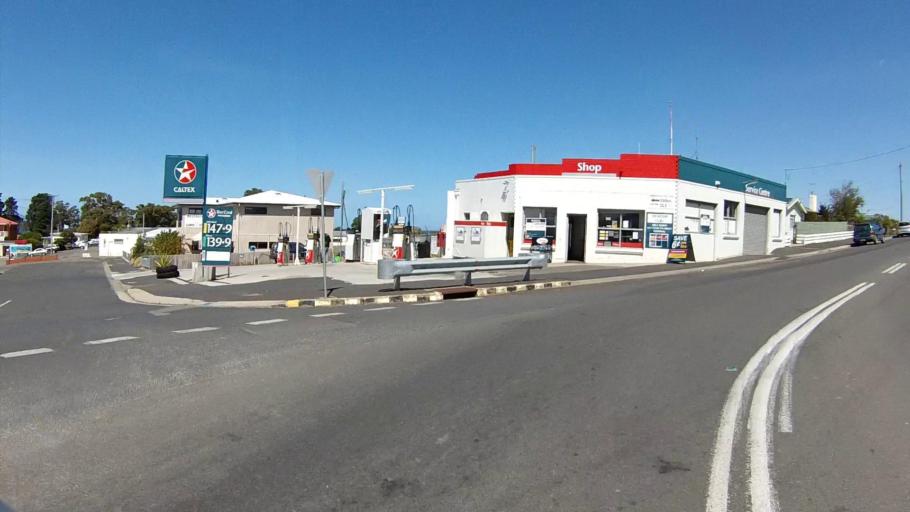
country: AU
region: Tasmania
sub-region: Break O'Day
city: St Helens
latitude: -42.1248
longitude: 148.0776
